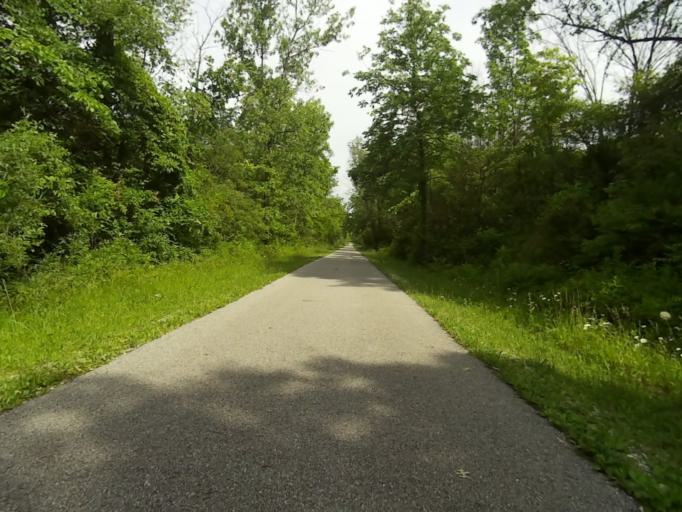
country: US
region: Ohio
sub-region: Summit County
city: Boston Heights
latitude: 41.2896
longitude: -81.5430
